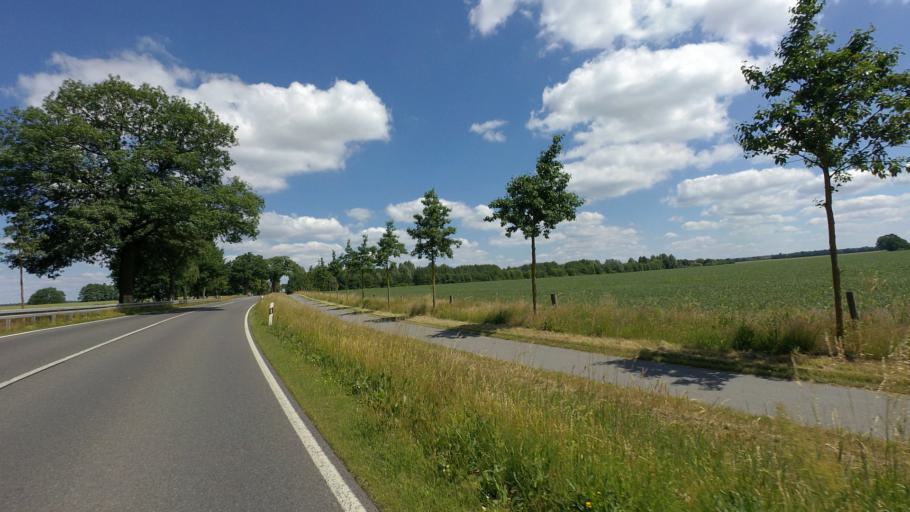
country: DE
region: Brandenburg
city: Sonnewalde
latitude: 51.6731
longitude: 13.6418
